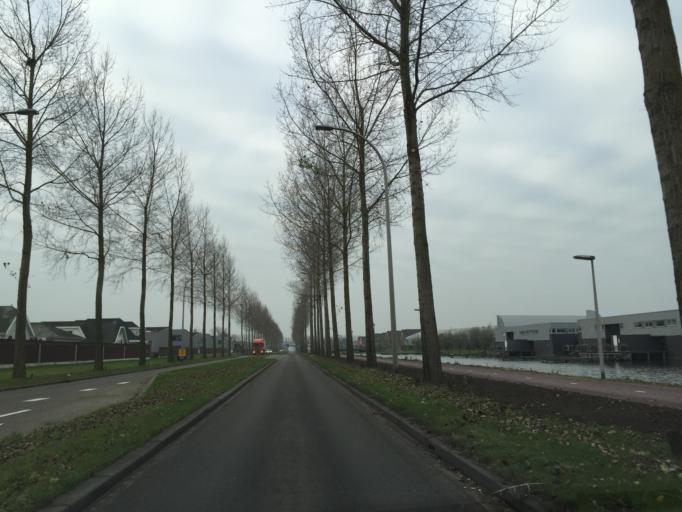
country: NL
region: South Holland
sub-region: Gemeente Den Haag
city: Ypenburg
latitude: 52.0334
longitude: 4.3701
